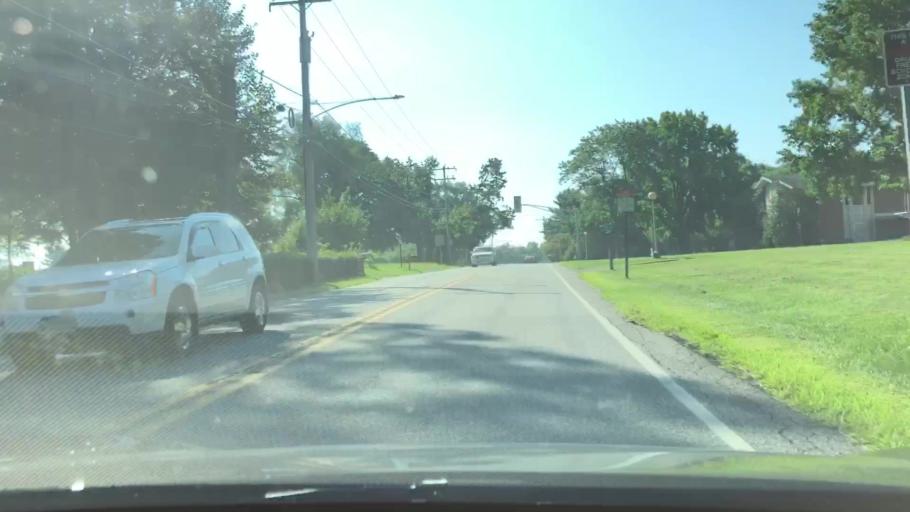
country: US
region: Pennsylvania
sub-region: Montgomery County
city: Dresher
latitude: 40.1528
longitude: -75.1726
